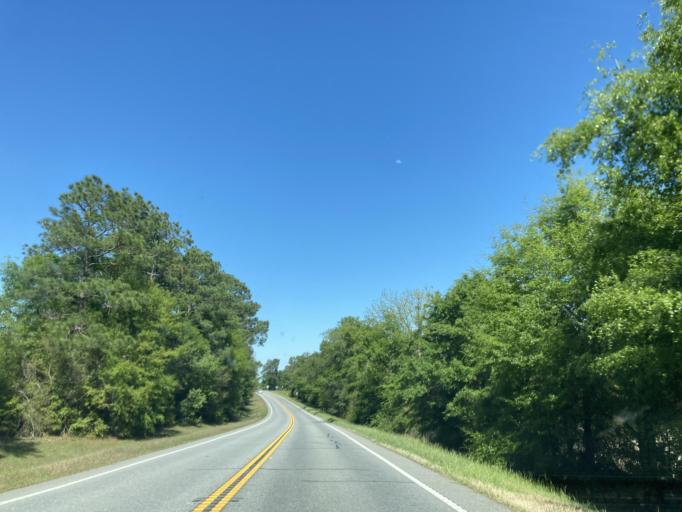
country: US
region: Georgia
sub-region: Miller County
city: Colquitt
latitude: 31.1892
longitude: -84.5212
